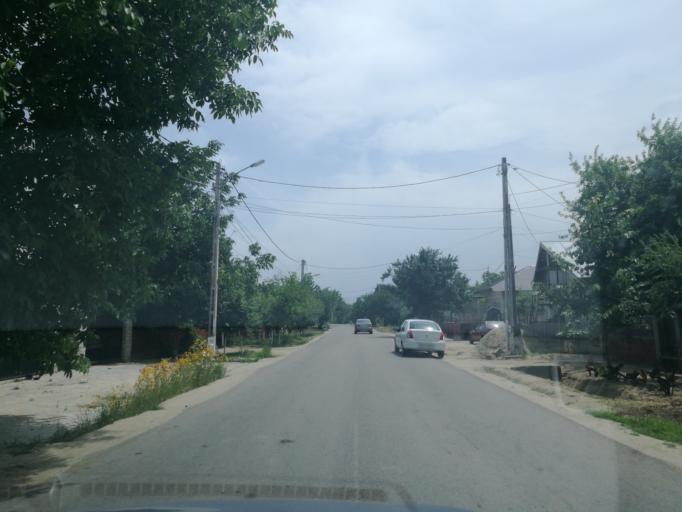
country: RO
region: Ilfov
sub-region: Comuna Vidra
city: Cretesti
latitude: 44.2750
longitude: 26.1381
